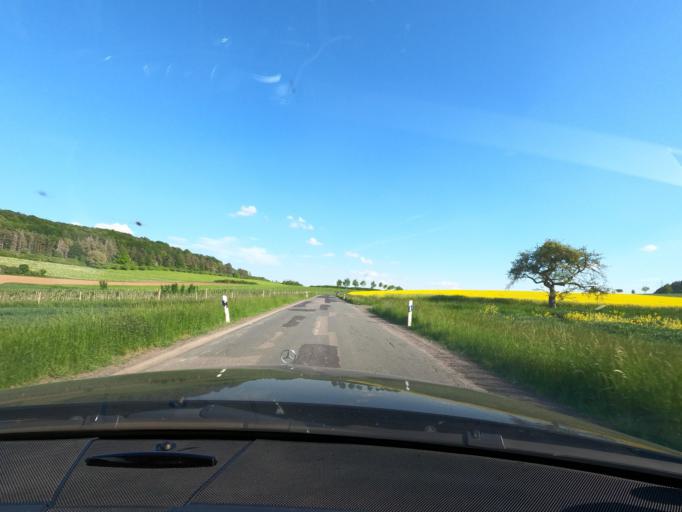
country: DE
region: Hesse
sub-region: Regierungsbezirk Kassel
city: Wolfhagen
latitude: 51.3619
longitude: 9.2065
